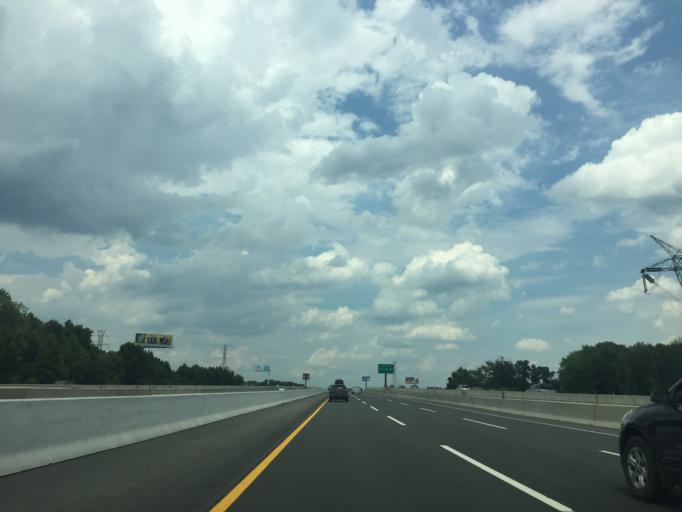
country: US
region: New Jersey
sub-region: Burlington County
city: Bordentown
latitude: 40.1145
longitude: -74.7121
